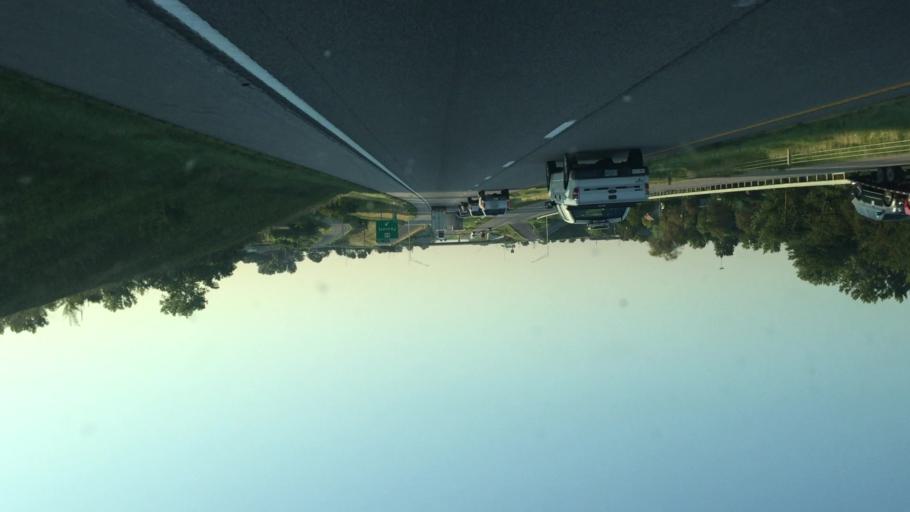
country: US
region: Kansas
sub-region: Doniphan County
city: Elwood
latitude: 39.5943
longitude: -94.7887
